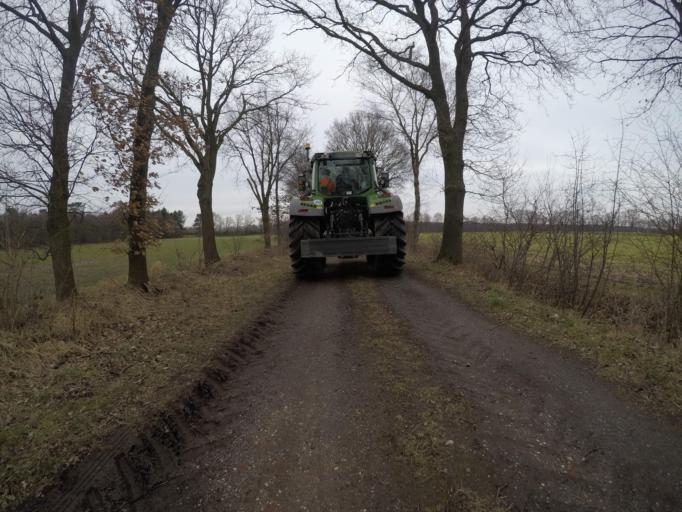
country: DE
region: North Rhine-Westphalia
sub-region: Regierungsbezirk Munster
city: Rhede
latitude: 51.7600
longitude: 6.6733
